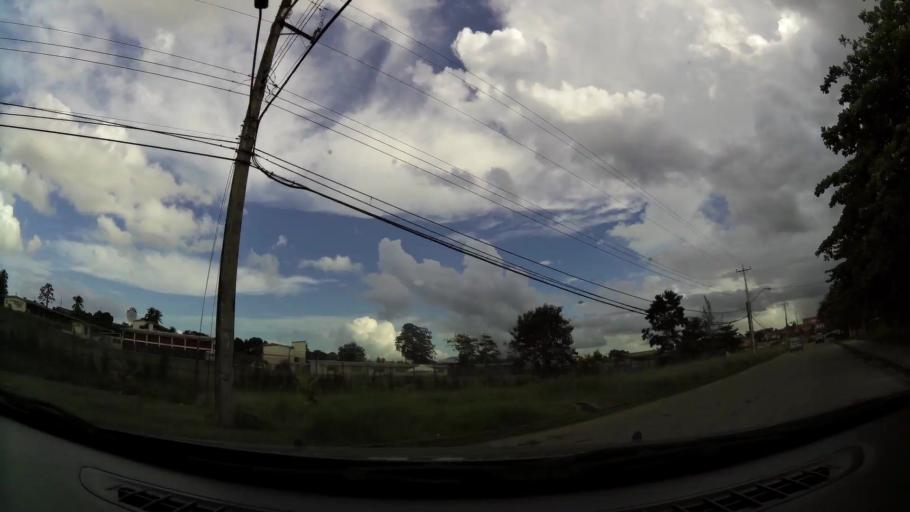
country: TT
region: City of San Fernando
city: Mon Repos
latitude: 10.2693
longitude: -61.4485
